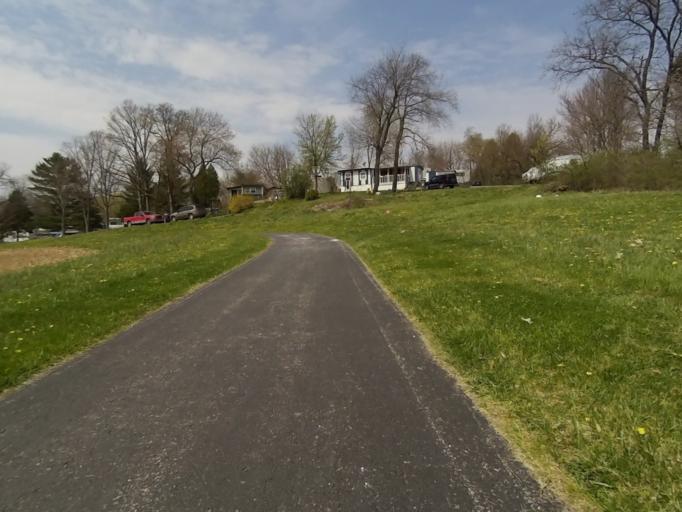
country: US
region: Pennsylvania
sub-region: Centre County
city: Park Forest Village
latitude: 40.7950
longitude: -77.8935
